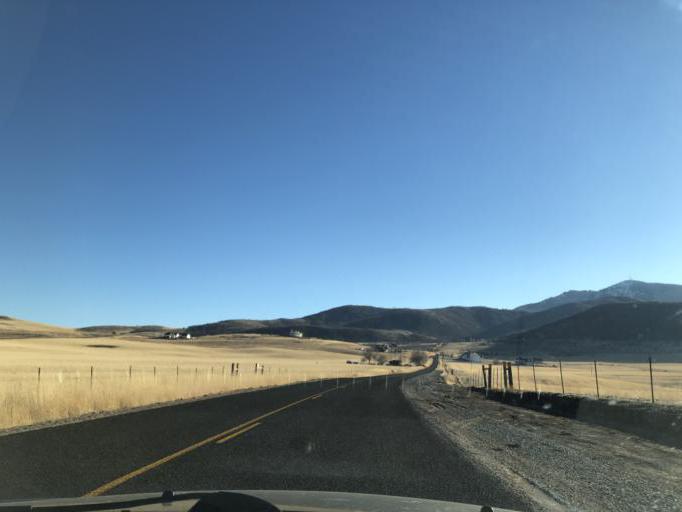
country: US
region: Utah
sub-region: Cache County
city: Wellsville
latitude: 41.5931
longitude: -111.9273
